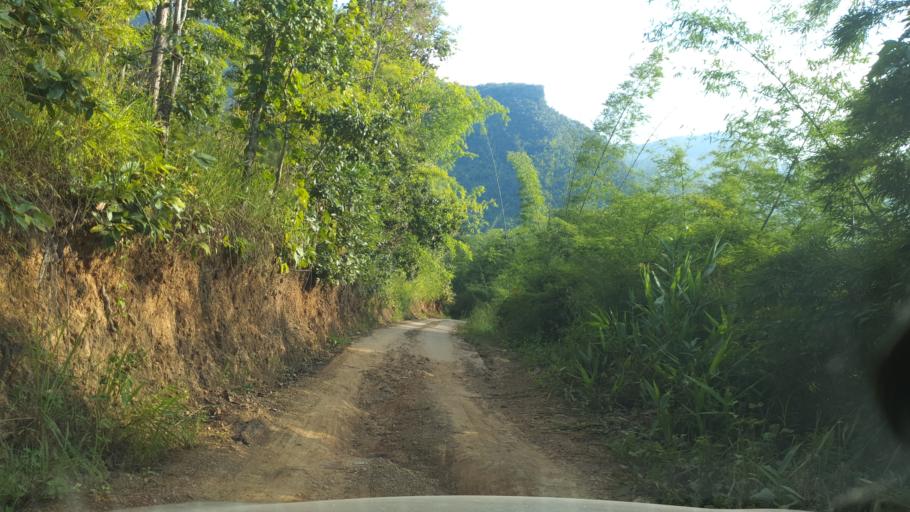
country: TH
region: Chiang Mai
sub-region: Amphoe Chiang Dao
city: Chiang Dao
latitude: 19.4094
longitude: 98.8323
